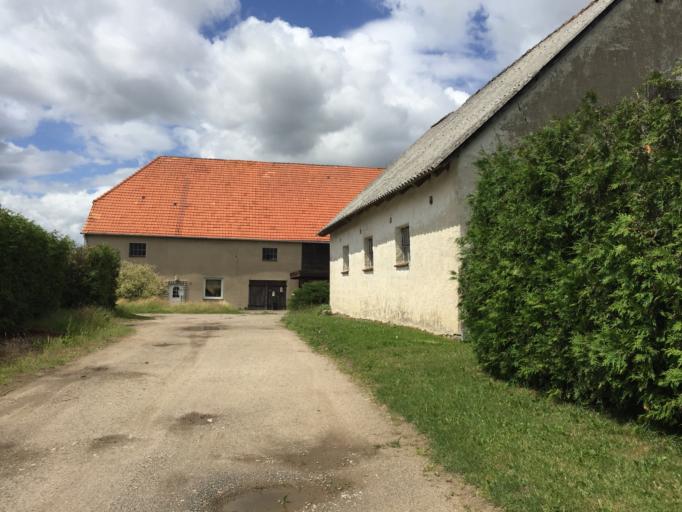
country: DE
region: Mecklenburg-Vorpommern
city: Wattmannshagen
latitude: 53.7764
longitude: 12.4164
